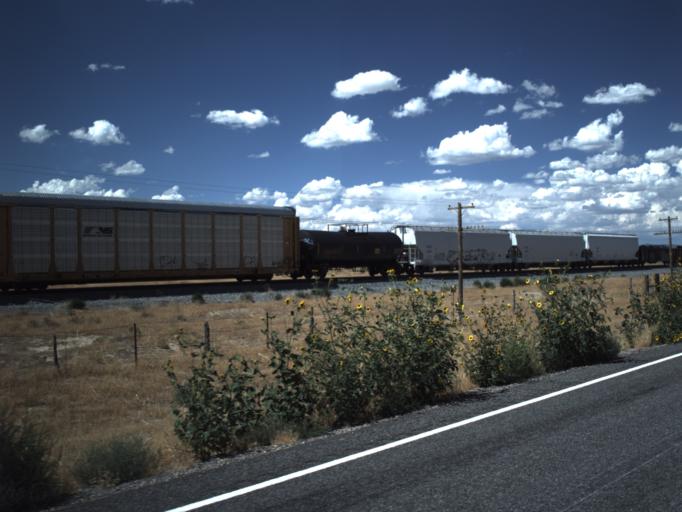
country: US
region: Utah
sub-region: Millard County
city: Delta
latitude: 39.5730
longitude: -112.3418
